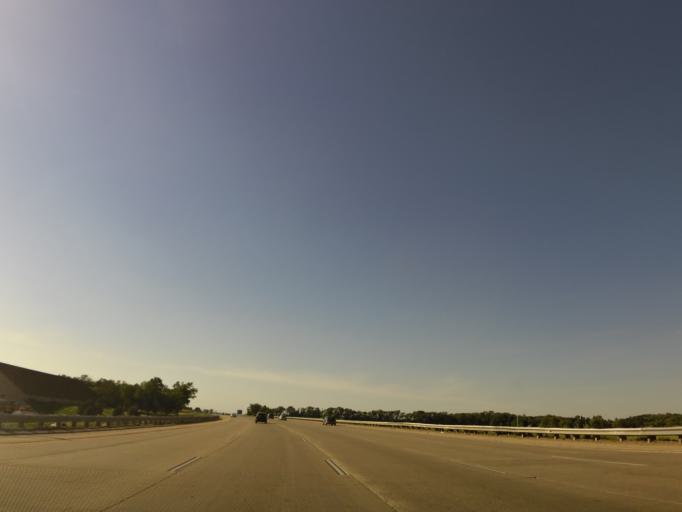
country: US
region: Wisconsin
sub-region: Dane County
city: Monona
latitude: 43.1075
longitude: -89.2828
